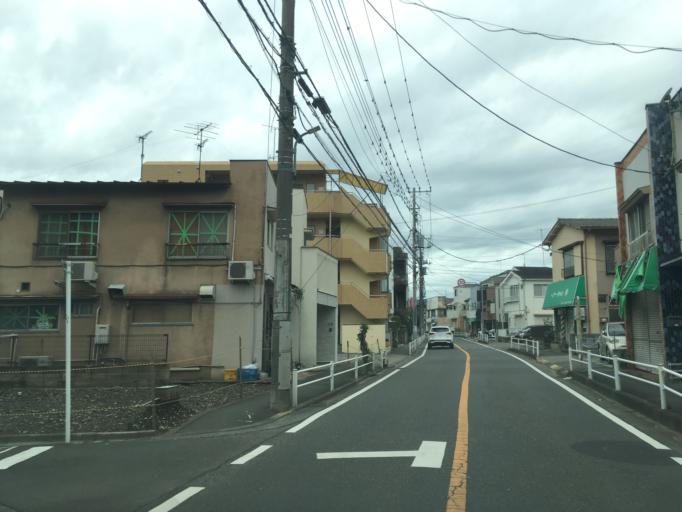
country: JP
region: Tokyo
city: Chofugaoka
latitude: 35.6241
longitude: 139.5775
